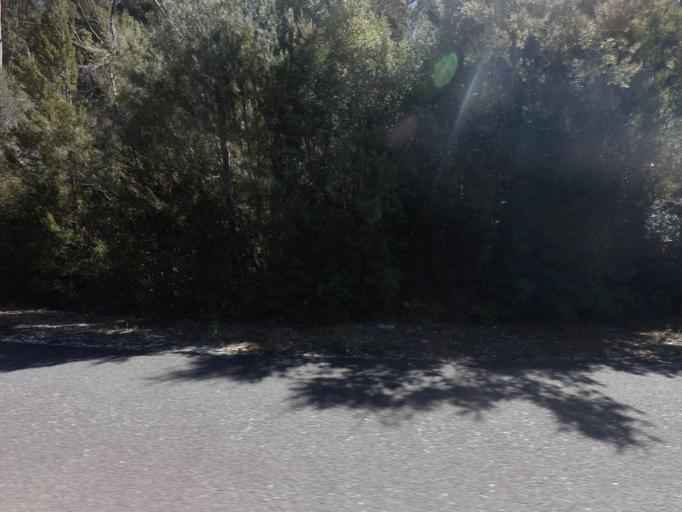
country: AU
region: Tasmania
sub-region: West Coast
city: Queenstown
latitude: -42.7644
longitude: 146.0056
